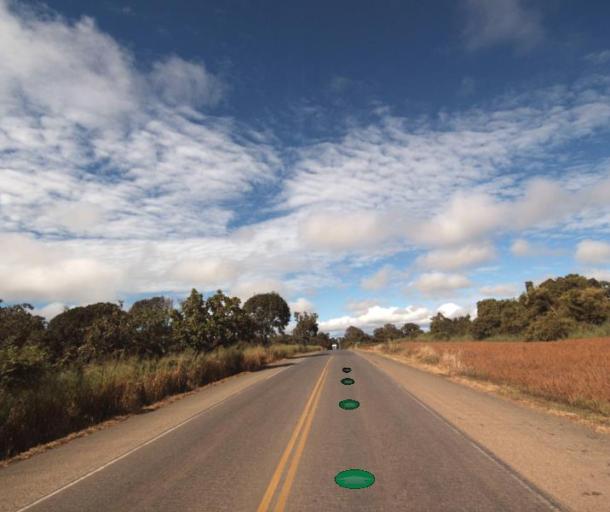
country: BR
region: Goias
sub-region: Uruacu
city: Uruacu
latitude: -14.6643
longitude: -49.1953
